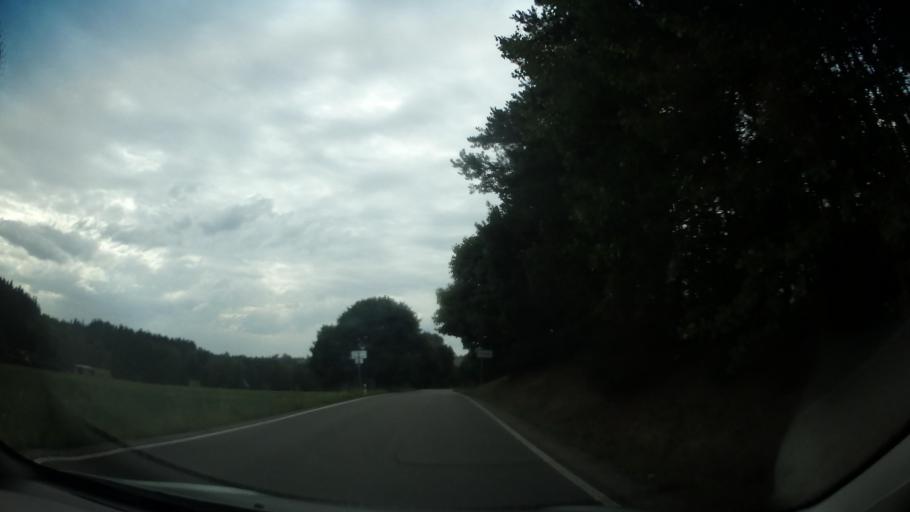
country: CZ
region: Pardubicky
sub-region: Okres Chrudim
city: Nasavrky
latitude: 49.7986
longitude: 15.7764
